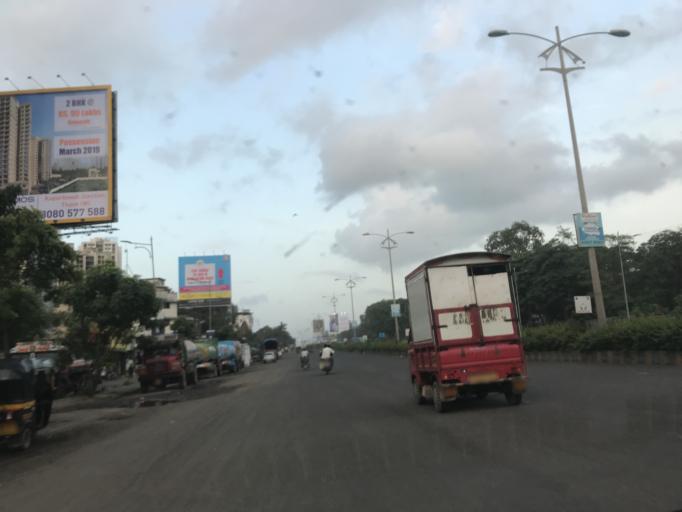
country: IN
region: Maharashtra
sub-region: Thane
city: Thane
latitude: 19.2194
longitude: 72.9854
